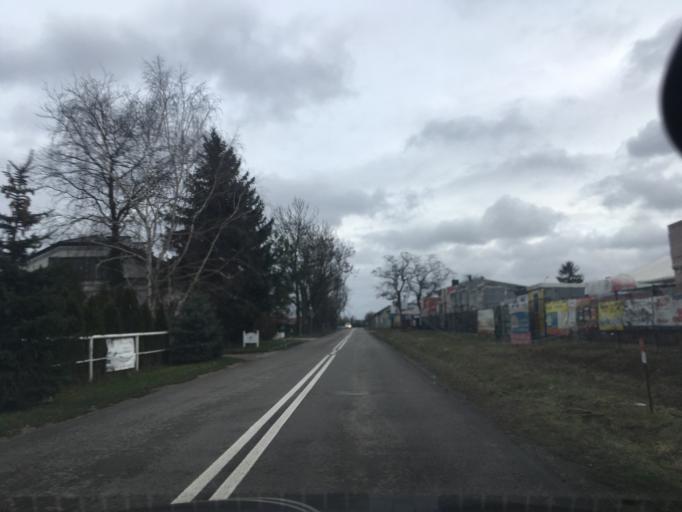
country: PL
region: Masovian Voivodeship
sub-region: Powiat piaseczynski
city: Lesznowola
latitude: 52.1199
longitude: 20.9396
